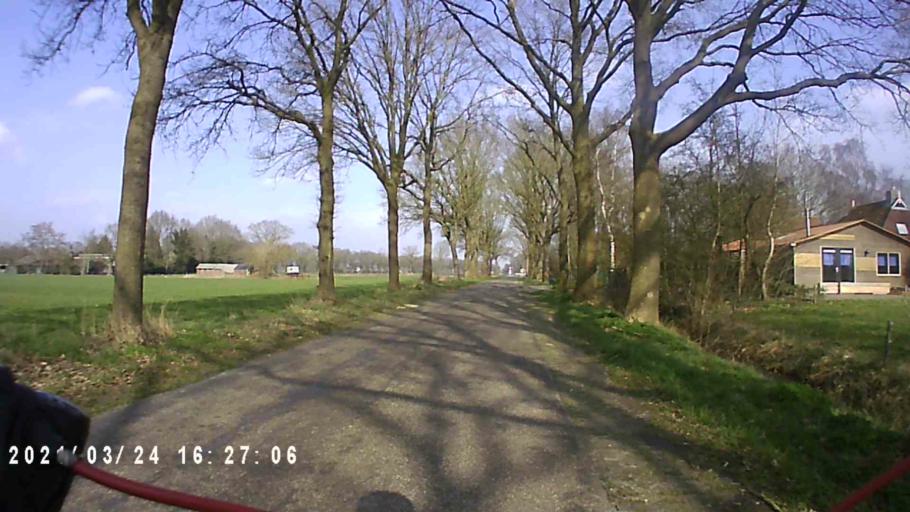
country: NL
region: Groningen
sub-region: Gemeente Leek
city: Leek
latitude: 53.0654
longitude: 6.2716
